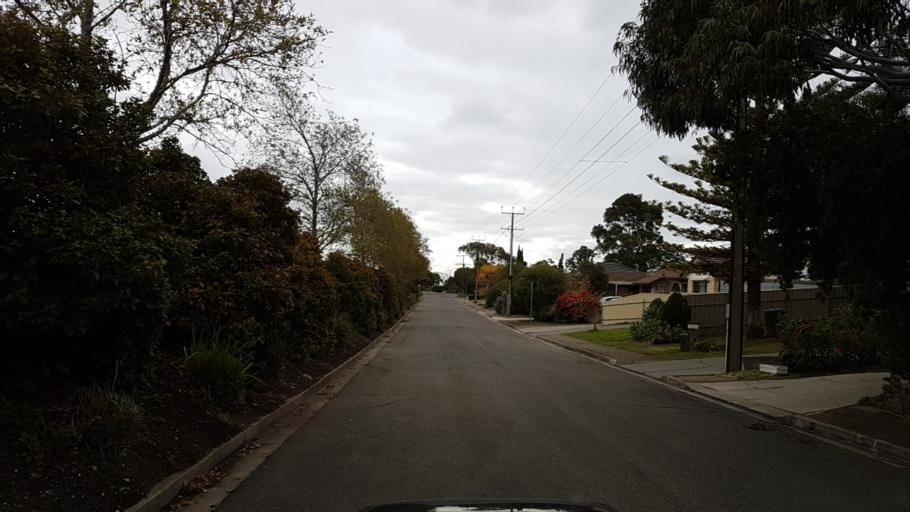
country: AU
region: South Australia
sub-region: Onkaparinga
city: Bedford Park
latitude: -35.0443
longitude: 138.5706
